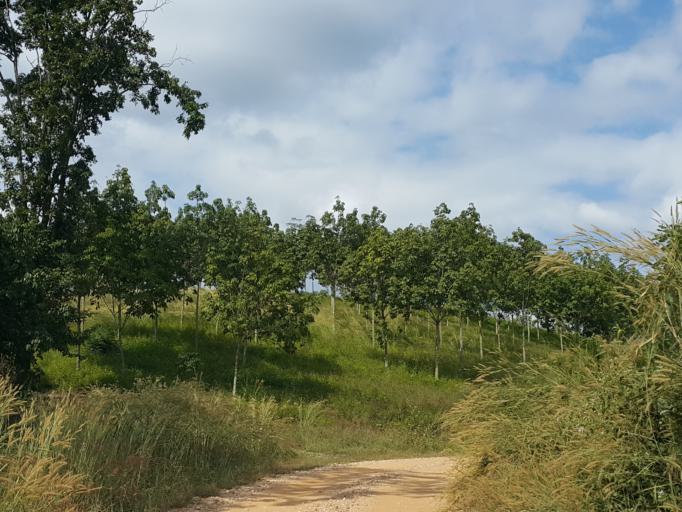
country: TH
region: Lampang
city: Hang Chat
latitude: 18.4832
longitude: 99.4153
